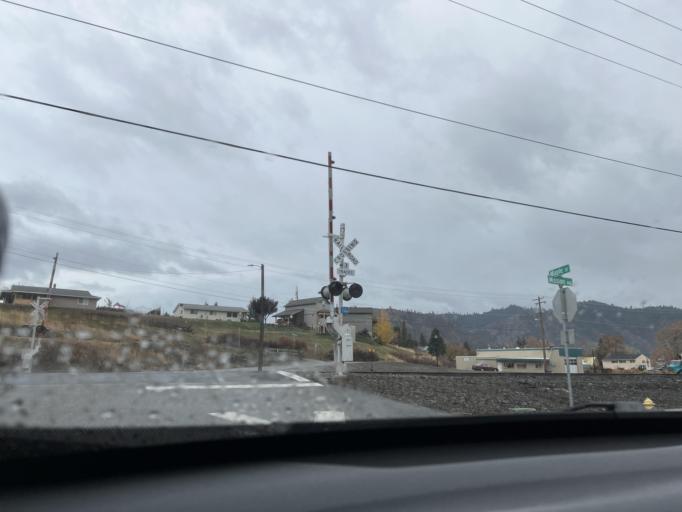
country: US
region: Washington
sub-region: Chelan County
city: Cashmere
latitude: 47.5207
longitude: -120.4656
